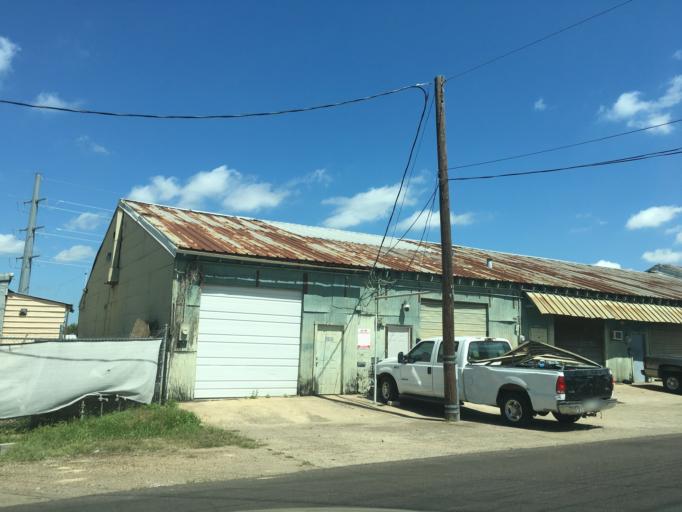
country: US
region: Texas
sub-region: Dallas County
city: Garland
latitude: 32.8353
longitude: -96.6878
